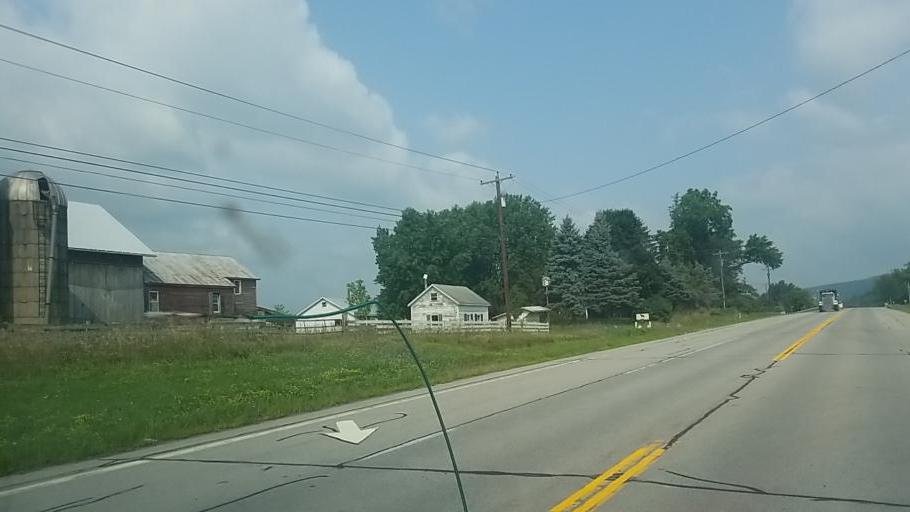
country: US
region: New York
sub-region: Montgomery County
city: Fort Plain
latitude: 42.9640
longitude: -74.6260
